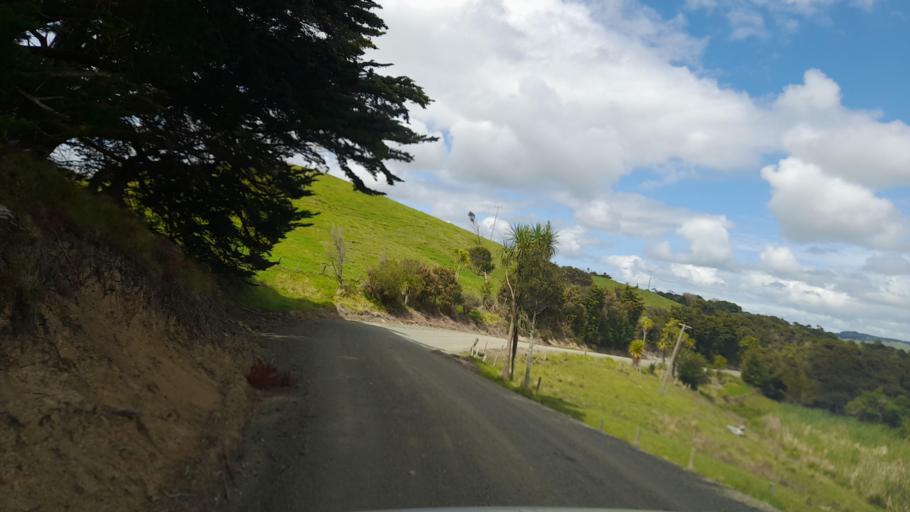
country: NZ
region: Auckland
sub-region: Auckland
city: Wellsford
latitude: -36.2041
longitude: 174.3371
